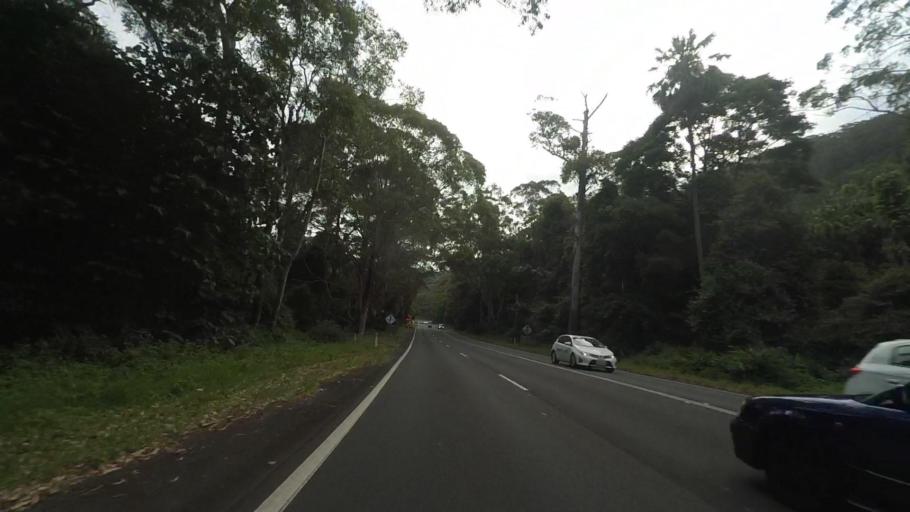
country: AU
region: New South Wales
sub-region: Wollongong
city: Bulli
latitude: -34.3190
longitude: 150.8971
